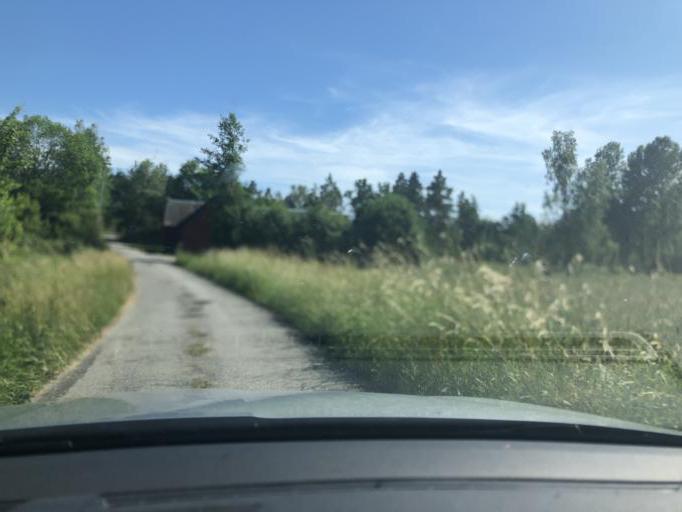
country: SE
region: Blekinge
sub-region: Karlshamns Kommun
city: Morrum
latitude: 56.1819
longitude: 14.7015
